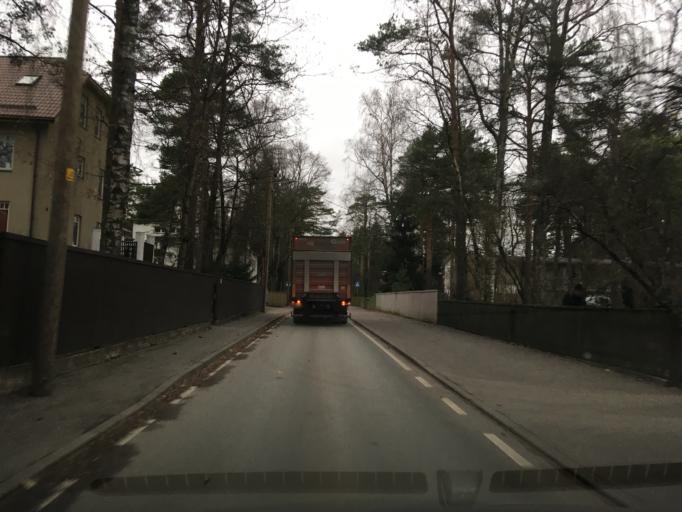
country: EE
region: Harju
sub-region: Saue vald
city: Laagri
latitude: 59.3790
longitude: 24.6756
